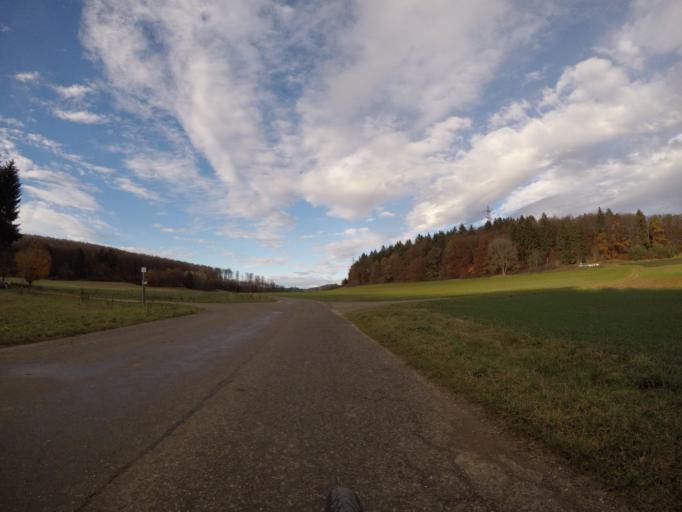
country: DE
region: Baden-Wuerttemberg
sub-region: Tuebingen Region
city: Sankt Johann
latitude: 48.4563
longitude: 9.3178
